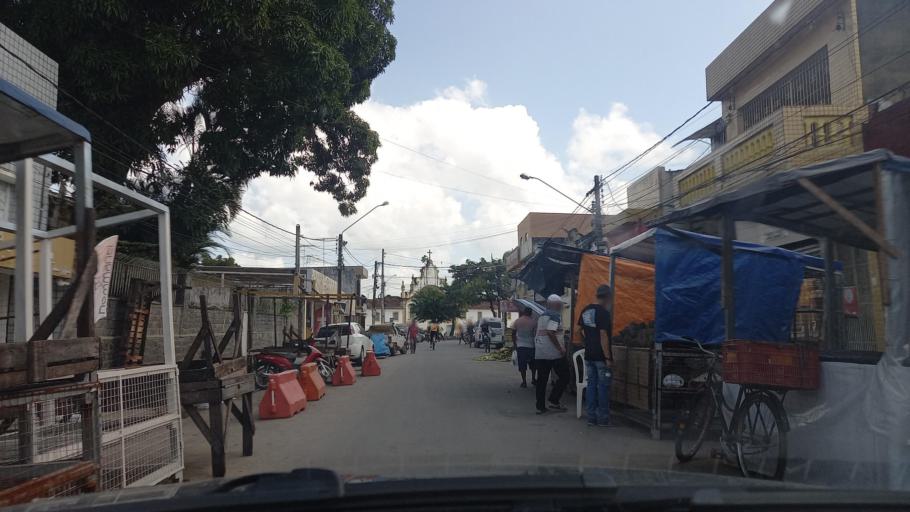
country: BR
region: Pernambuco
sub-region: Goiana
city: Goiana
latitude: -7.5614
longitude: -35.0012
